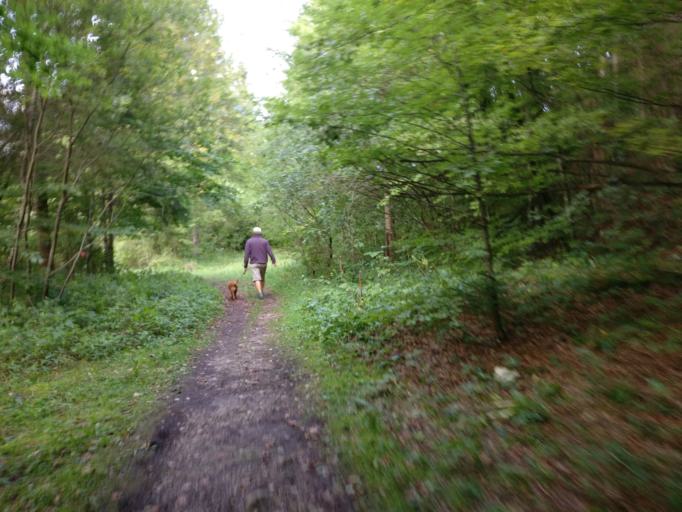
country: SI
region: Kranjska Gora
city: Mojstrana
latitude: 46.4543
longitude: 13.9334
